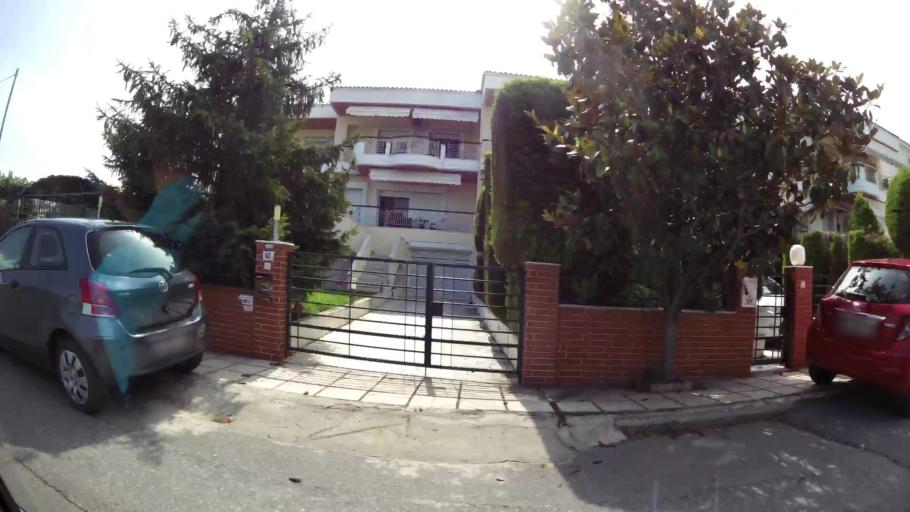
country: GR
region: Central Macedonia
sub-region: Nomos Thessalonikis
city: Panorama
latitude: 40.5823
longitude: 23.0133
